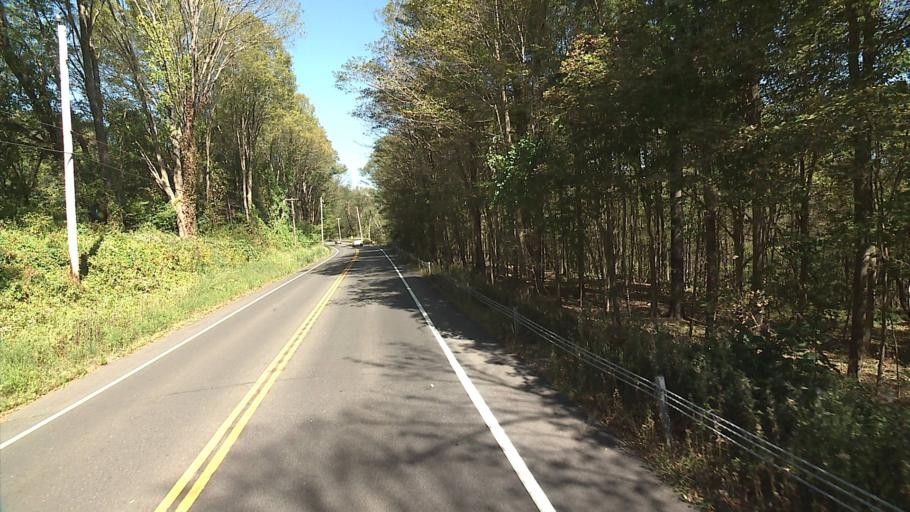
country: US
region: Connecticut
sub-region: New Haven County
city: Woodbridge
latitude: 41.4208
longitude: -72.9724
